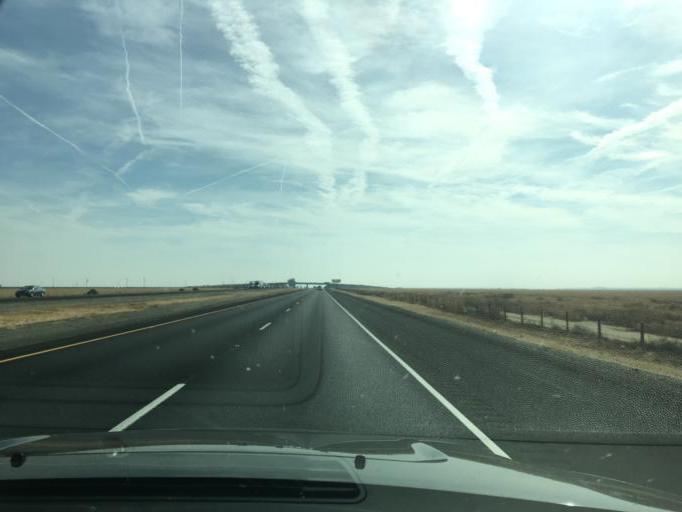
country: US
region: California
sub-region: Kern County
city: Lost Hills
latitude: 35.6730
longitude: -119.6957
